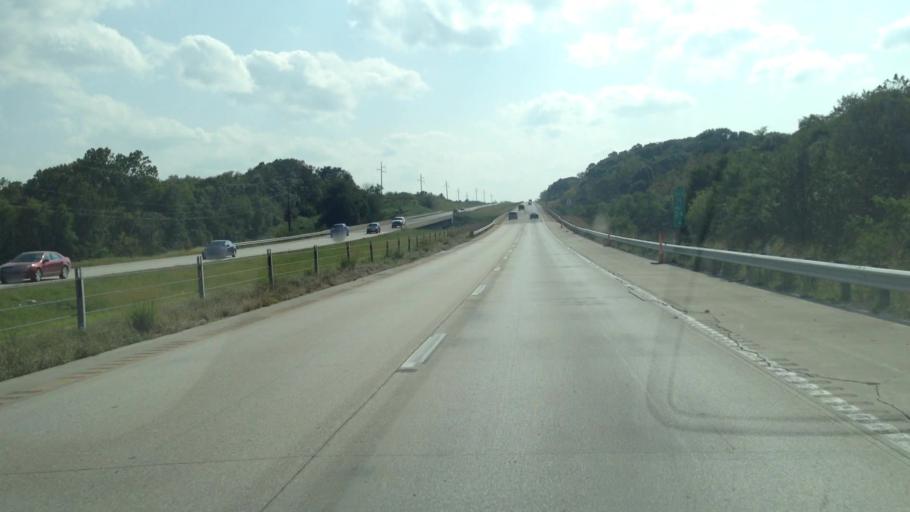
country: US
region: Missouri
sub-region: Clay County
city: Kearney
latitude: 39.3476
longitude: -94.3834
